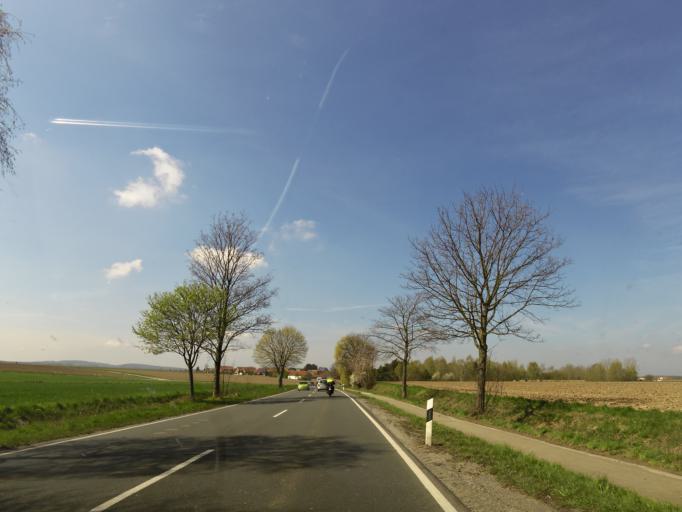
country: DE
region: Lower Saxony
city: Hagenburg
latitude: 52.4354
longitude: 9.3614
